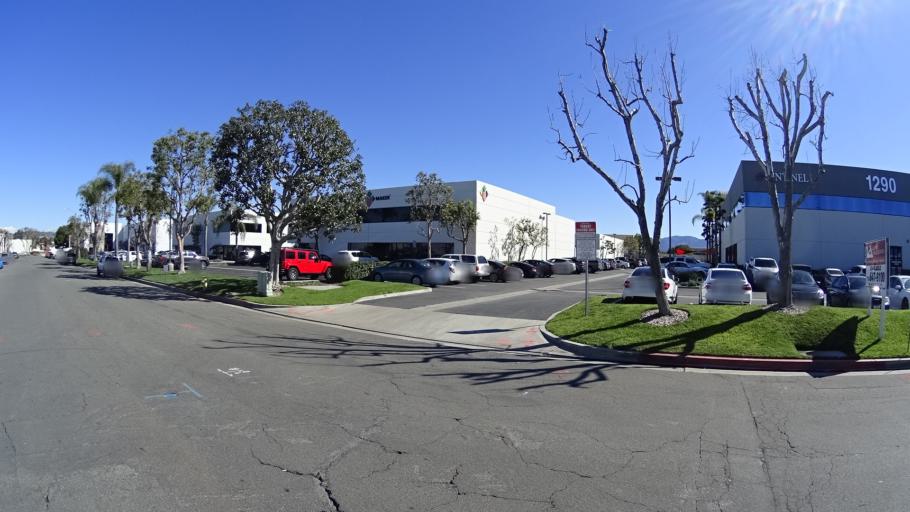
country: US
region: California
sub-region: Orange County
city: Yorba Linda
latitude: 33.8625
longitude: -117.8144
